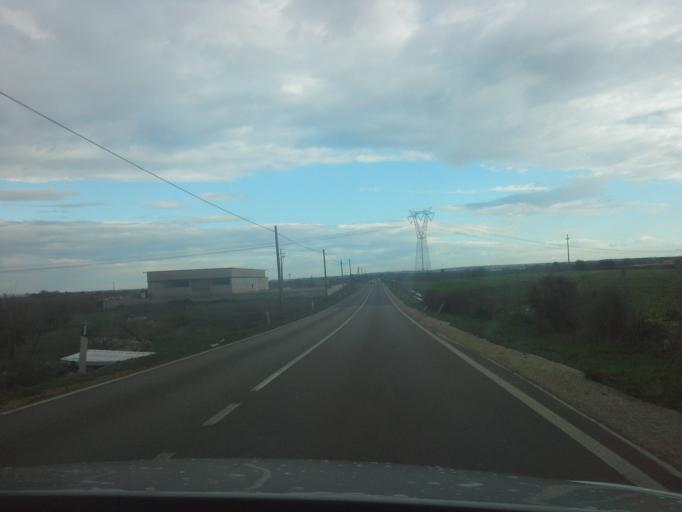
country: IT
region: Apulia
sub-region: Provincia di Bari
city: Casamassima
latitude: 40.9407
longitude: 16.9574
